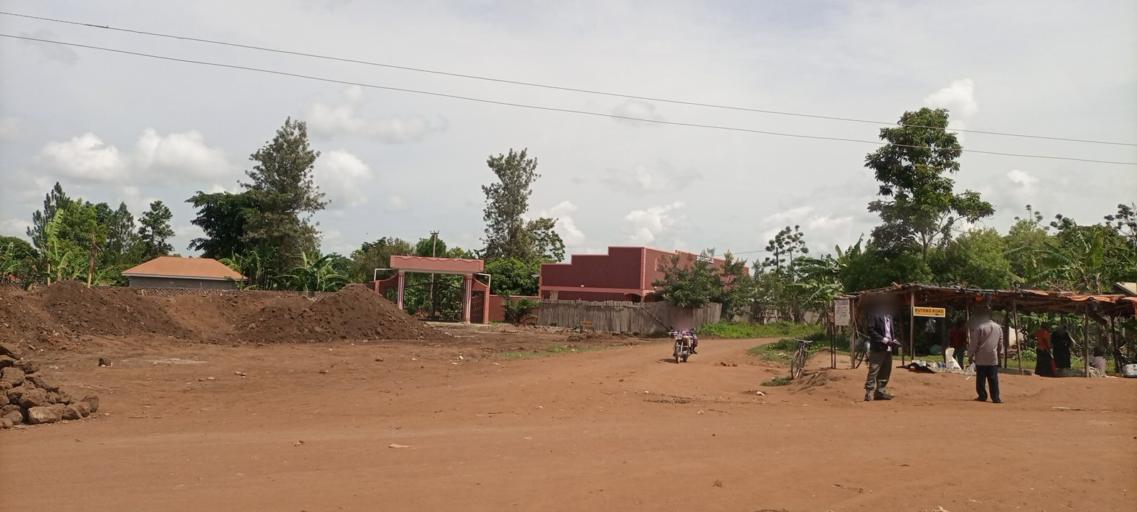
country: UG
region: Eastern Region
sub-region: Budaka District
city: Budaka
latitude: 1.1719
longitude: 33.9332
